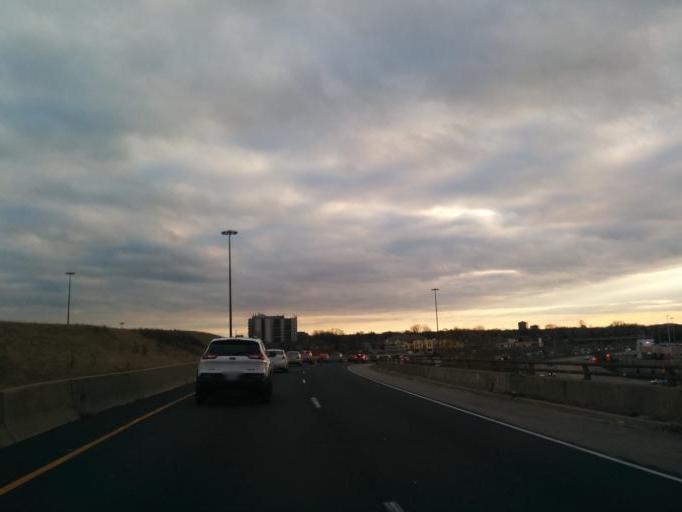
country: CA
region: Ontario
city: Etobicoke
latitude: 43.6146
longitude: -79.5516
